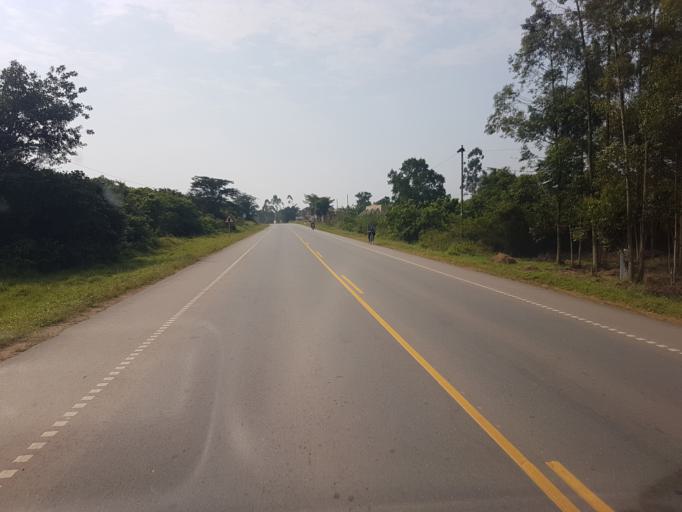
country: UG
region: Western Region
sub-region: Mbarara District
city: Bwizibwera
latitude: -0.6419
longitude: 30.5580
